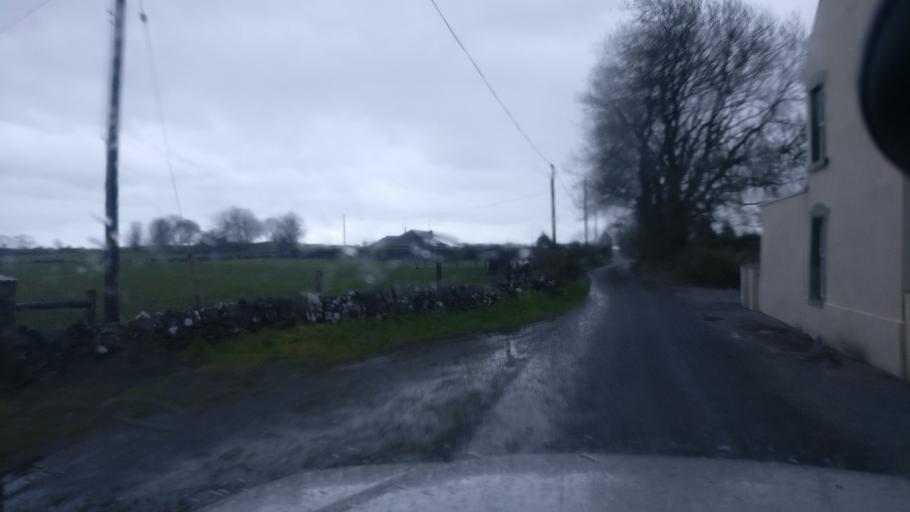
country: IE
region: Connaught
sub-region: County Galway
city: Loughrea
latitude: 53.2428
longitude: -8.4242
